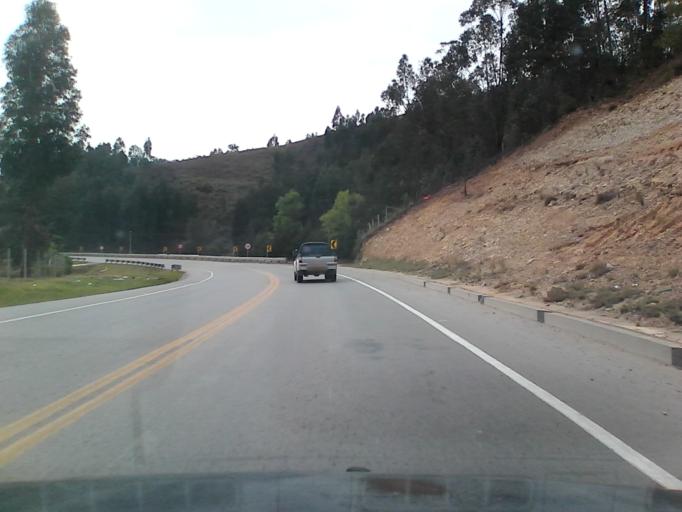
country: CO
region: Boyaca
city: Sogamoso
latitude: 5.7304
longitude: -72.9535
